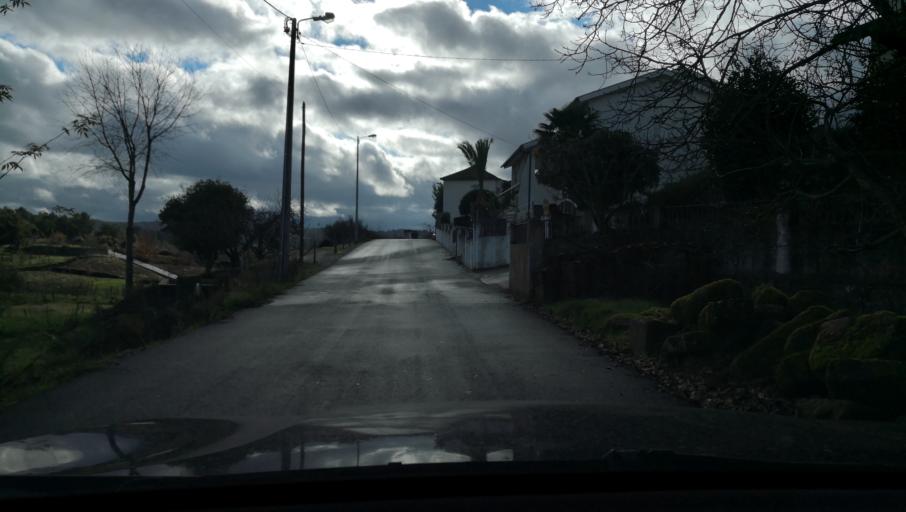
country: PT
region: Vila Real
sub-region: Vila Real
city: Vila Real
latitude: 41.2698
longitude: -7.7254
